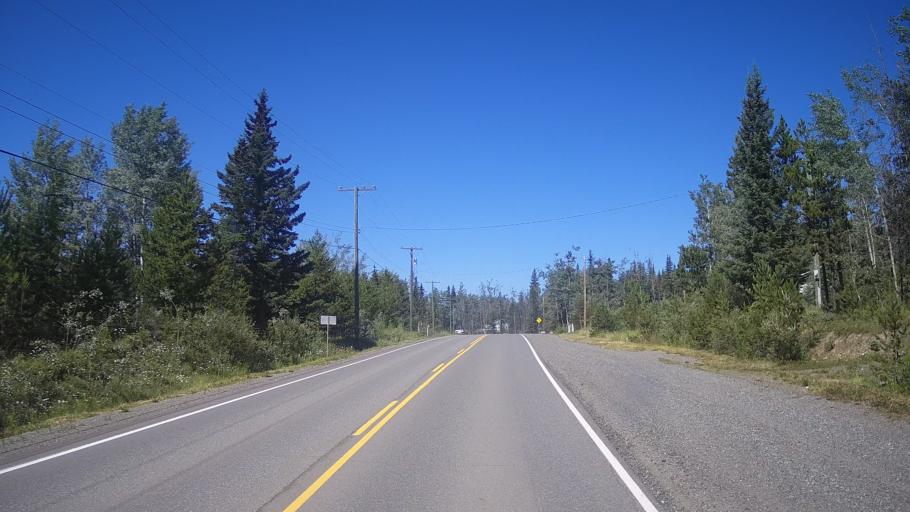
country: CA
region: British Columbia
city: Cache Creek
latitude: 51.5547
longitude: -121.2158
